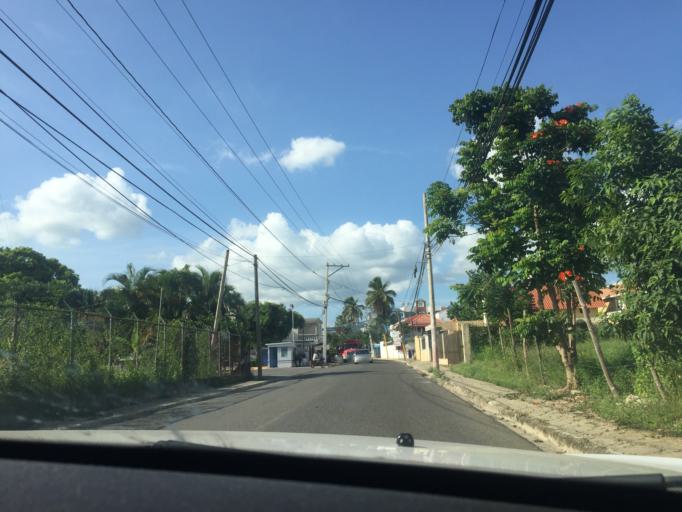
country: DO
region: Santiago
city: Santiago de los Caballeros
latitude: 19.4747
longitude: -70.6565
